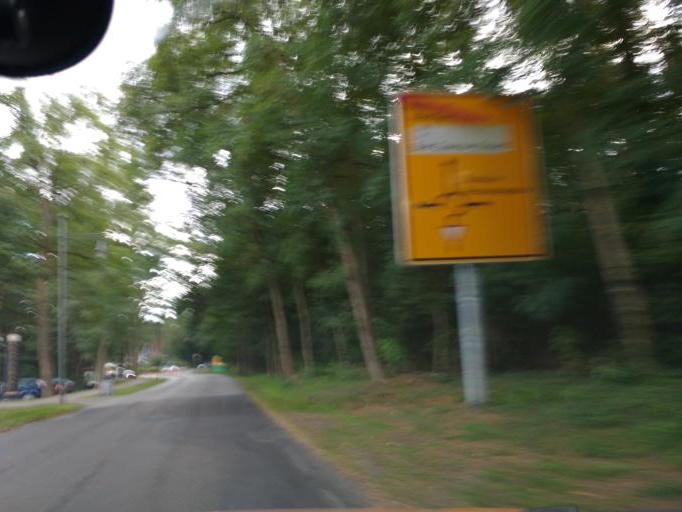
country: DE
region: Brandenburg
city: Diensdorf-Radlow
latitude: 52.2753
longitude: 14.0400
